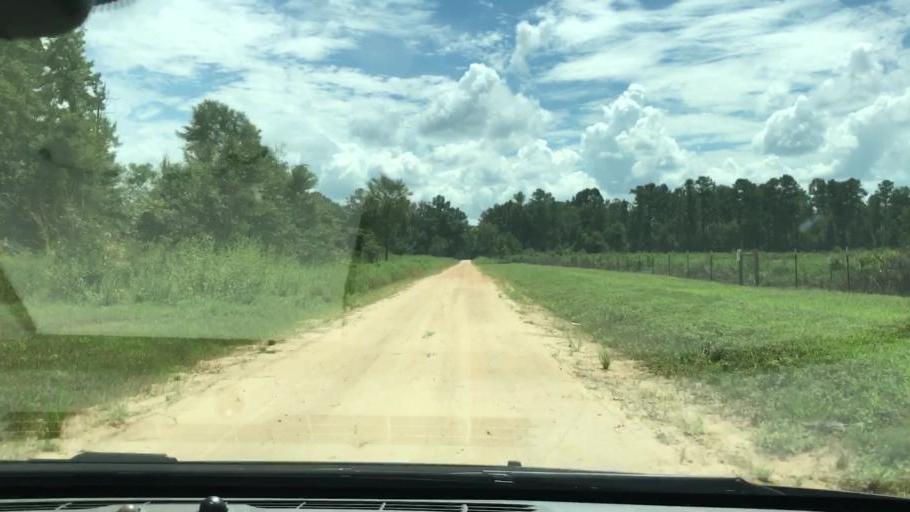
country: US
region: Georgia
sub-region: Quitman County
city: Georgetown
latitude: 32.0296
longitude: -85.0367
